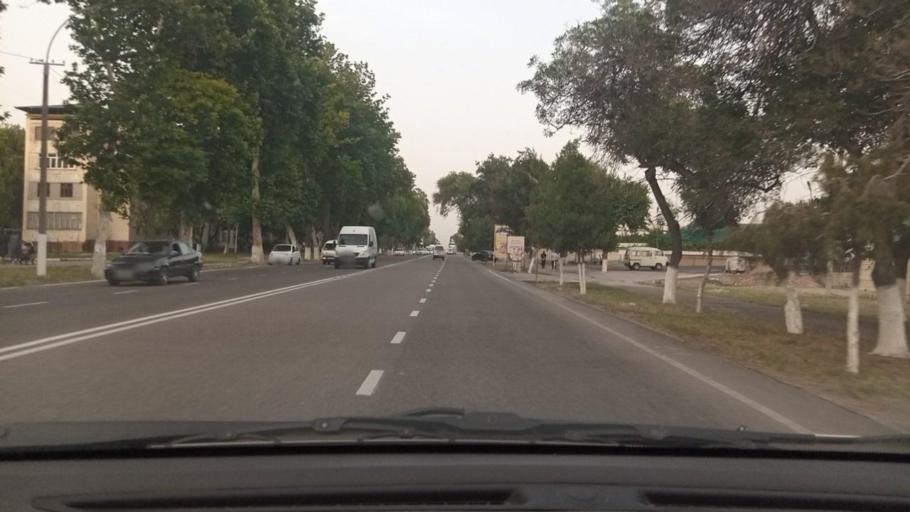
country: UZ
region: Toshkent
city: Angren
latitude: 41.0005
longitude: 70.0763
